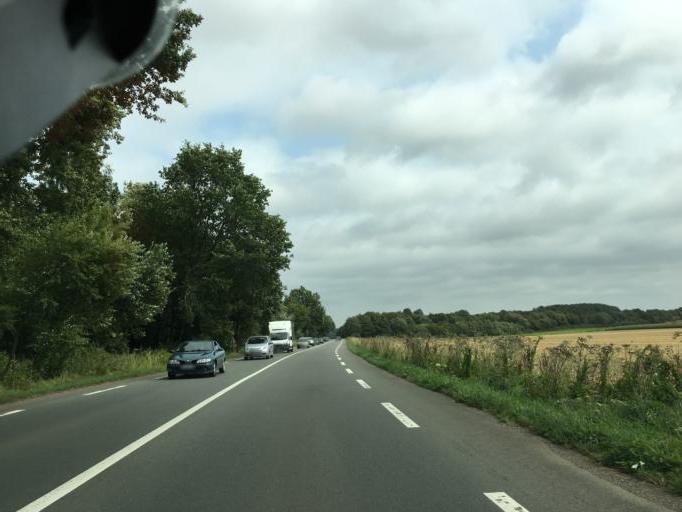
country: FR
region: Nord-Pas-de-Calais
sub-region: Departement du Pas-de-Calais
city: Pernes
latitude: 50.4236
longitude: 2.4266
